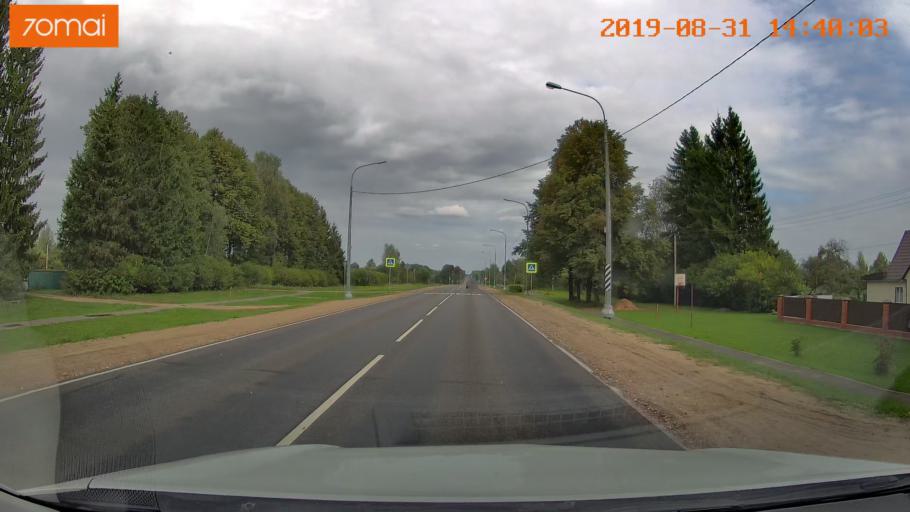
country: RU
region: Smolensk
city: Yekimovichi
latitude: 54.1951
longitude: 33.5645
